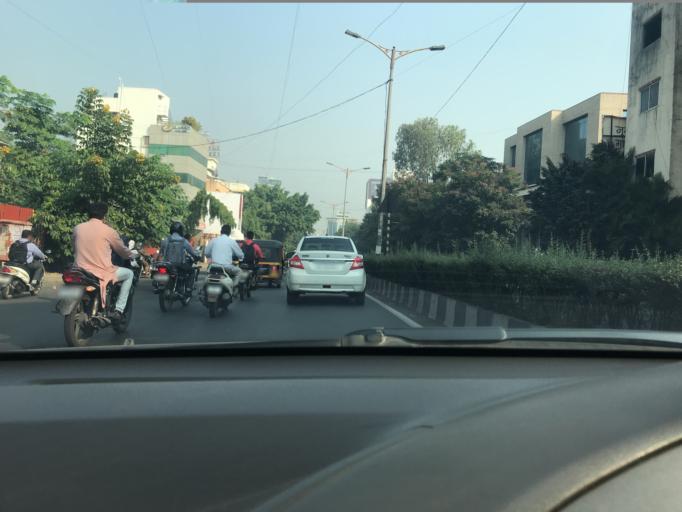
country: IN
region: Maharashtra
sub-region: Pune Division
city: Shivaji Nagar
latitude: 18.5261
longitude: 73.8297
